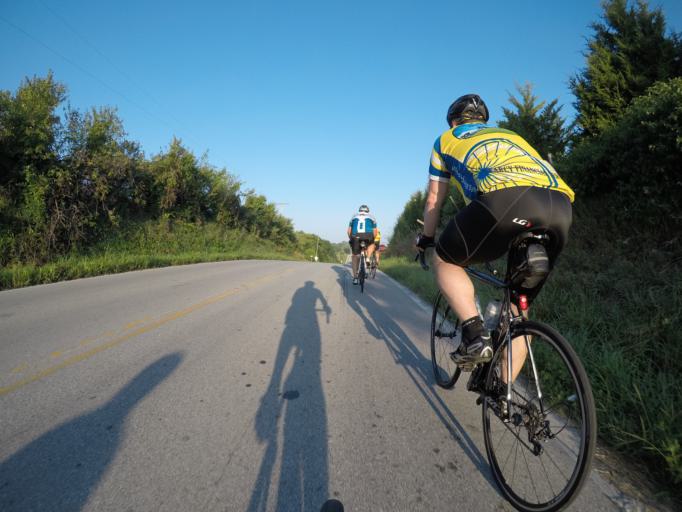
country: US
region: Kansas
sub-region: Leavenworth County
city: Lansing
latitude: 39.2159
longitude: -94.8623
